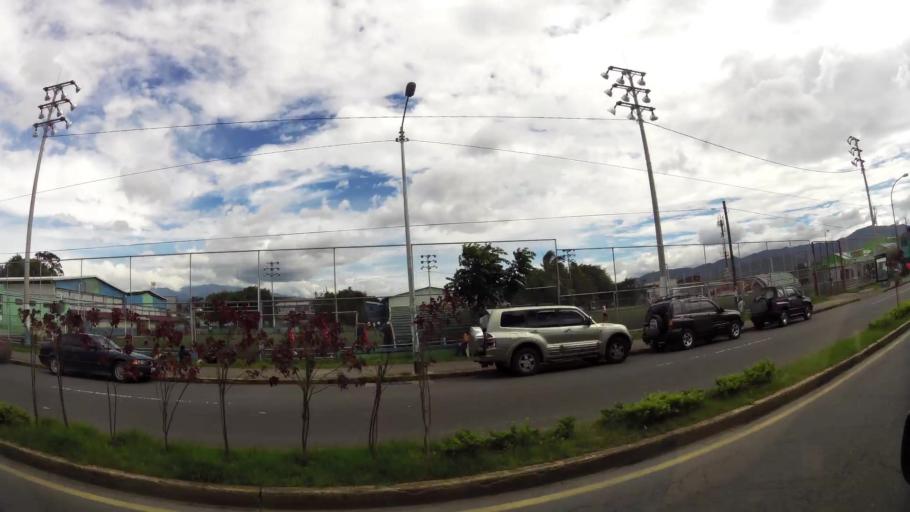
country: CR
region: San Jose
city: San Jose
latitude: 9.9243
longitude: -84.0749
